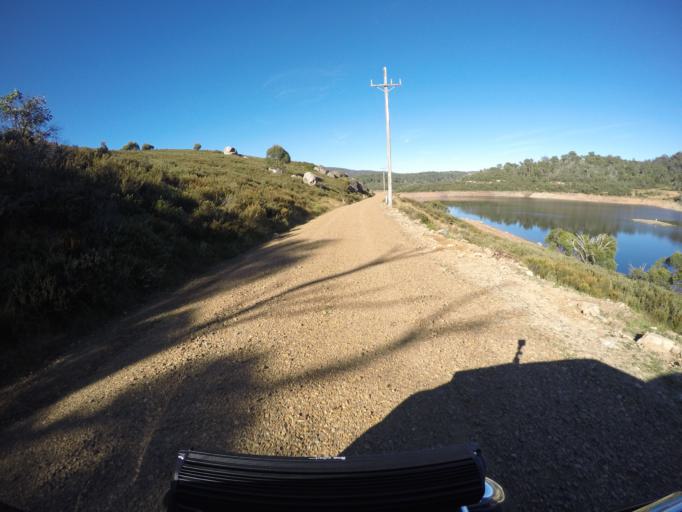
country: AU
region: New South Wales
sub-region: Snowy River
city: Jindabyne
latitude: -36.0536
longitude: 148.2796
